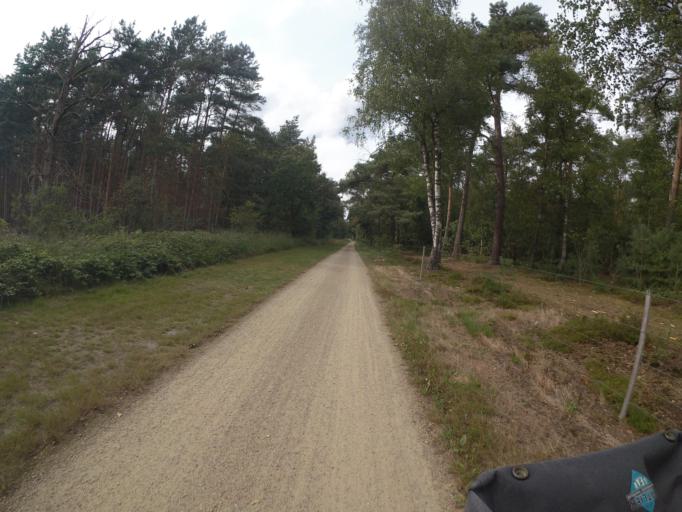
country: DE
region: North Rhine-Westphalia
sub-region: Regierungsbezirk Dusseldorf
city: Goch
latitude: 51.6202
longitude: 6.0729
